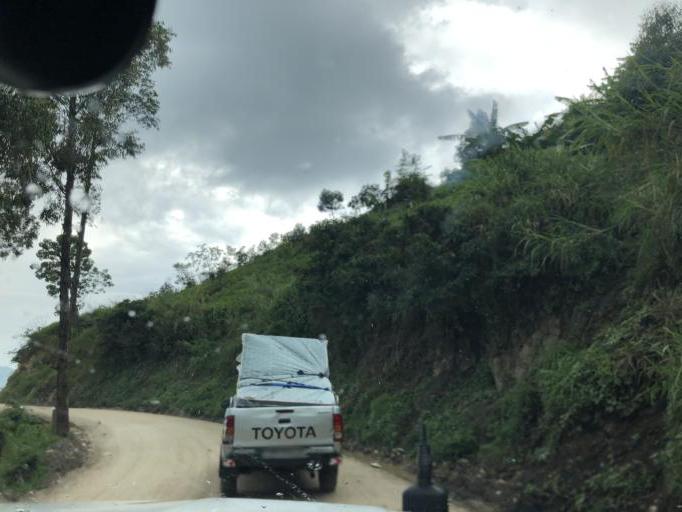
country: CD
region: Nord Kivu
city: Sake
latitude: -1.5848
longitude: 29.0473
